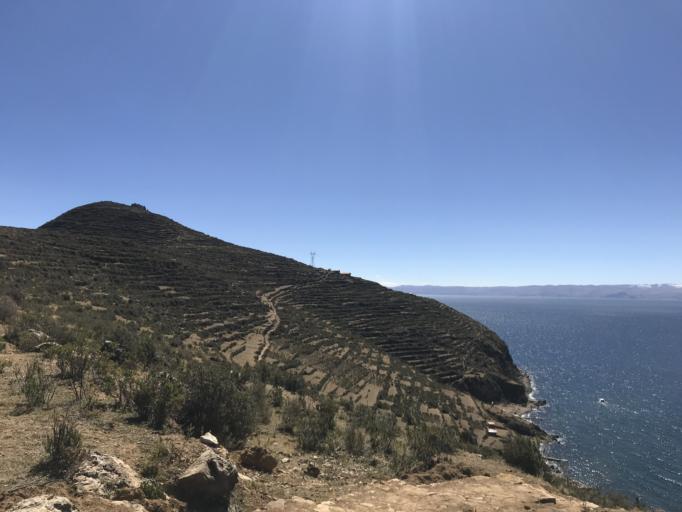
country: BO
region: La Paz
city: Yumani
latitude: -16.0495
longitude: -69.1454
